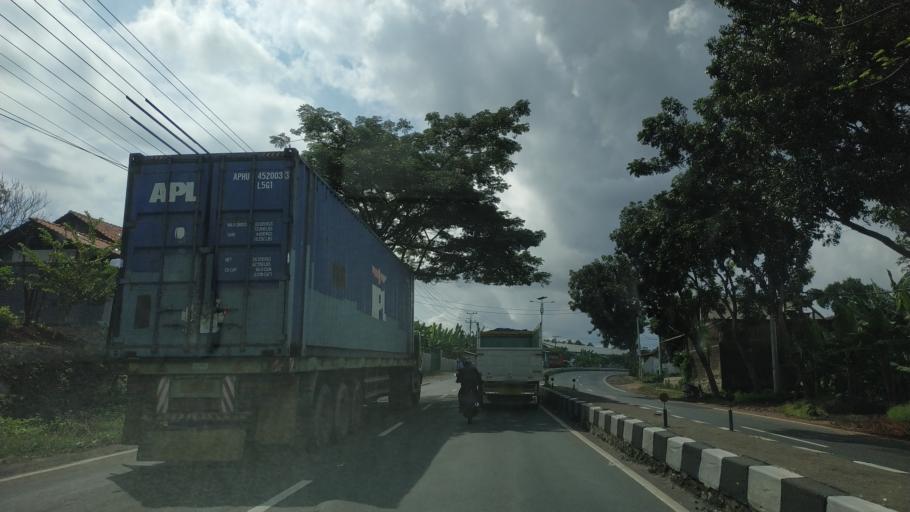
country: ID
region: Central Java
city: Pekalongan
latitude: -6.9464
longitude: 109.8228
